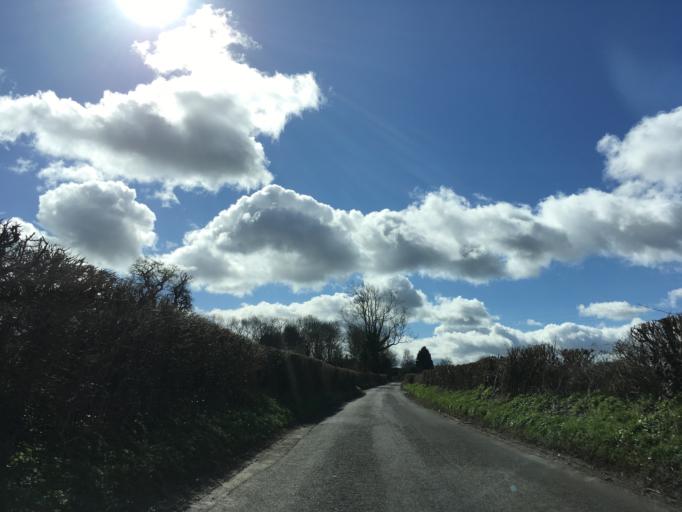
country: GB
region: England
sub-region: Gloucestershire
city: Wotton-under-Edge
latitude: 51.6098
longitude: -2.3346
